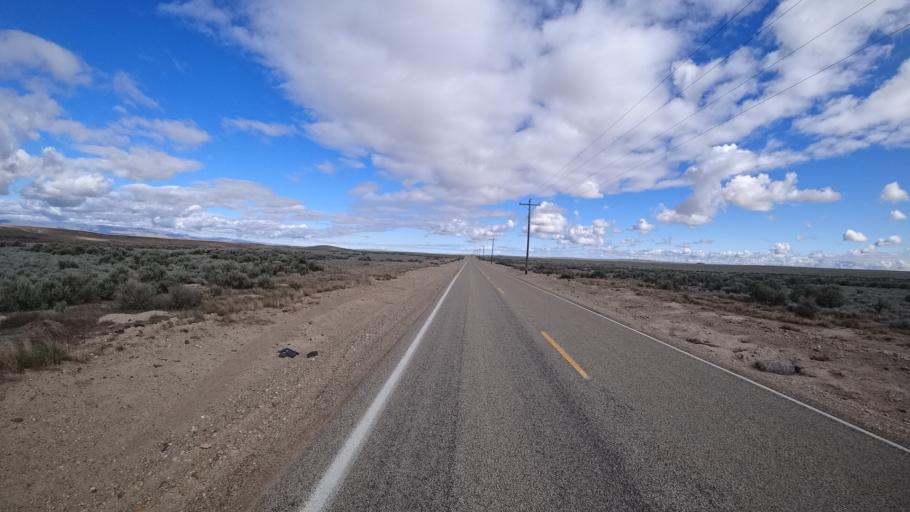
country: US
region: Idaho
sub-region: Owyhee County
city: Murphy
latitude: 43.2553
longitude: -116.3760
